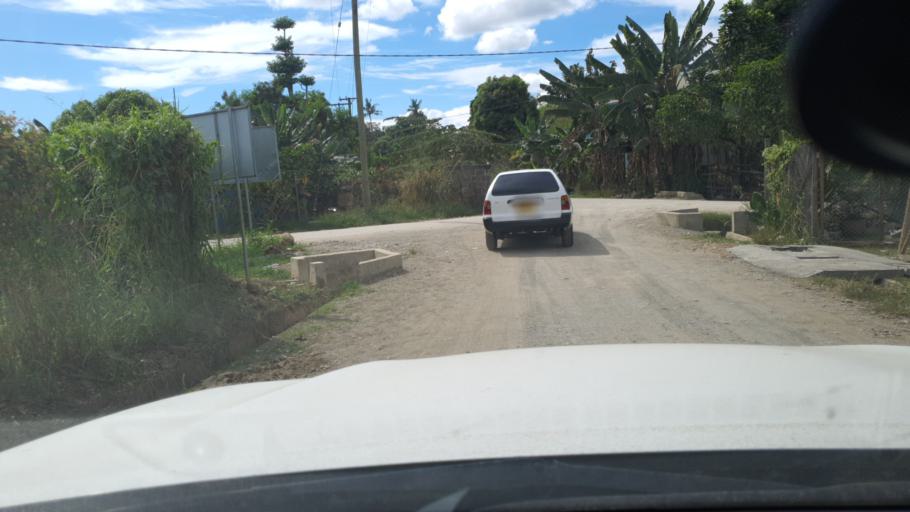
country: SB
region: Guadalcanal
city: Honiara
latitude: -9.4485
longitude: 159.9767
